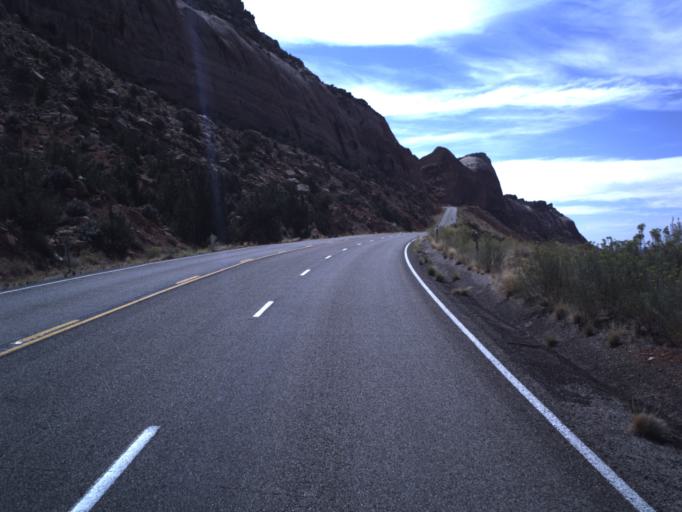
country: US
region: Utah
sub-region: San Juan County
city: Blanding
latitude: 37.5074
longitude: -109.6487
